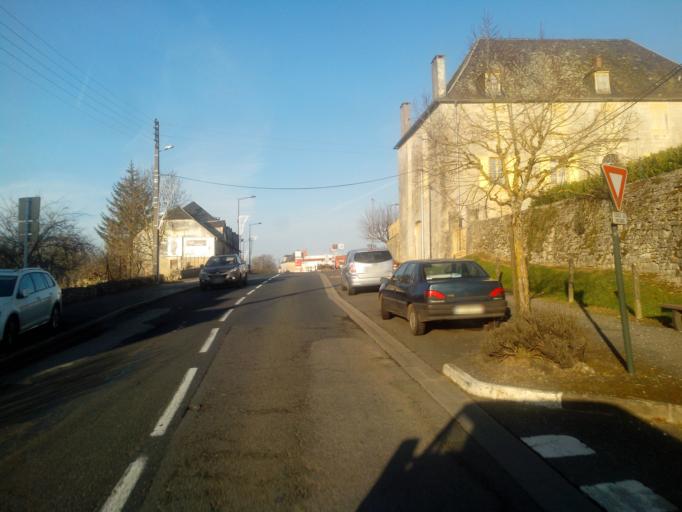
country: FR
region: Limousin
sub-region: Departement de la Correze
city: Brive-la-Gaillarde
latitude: 45.0210
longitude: 1.5199
